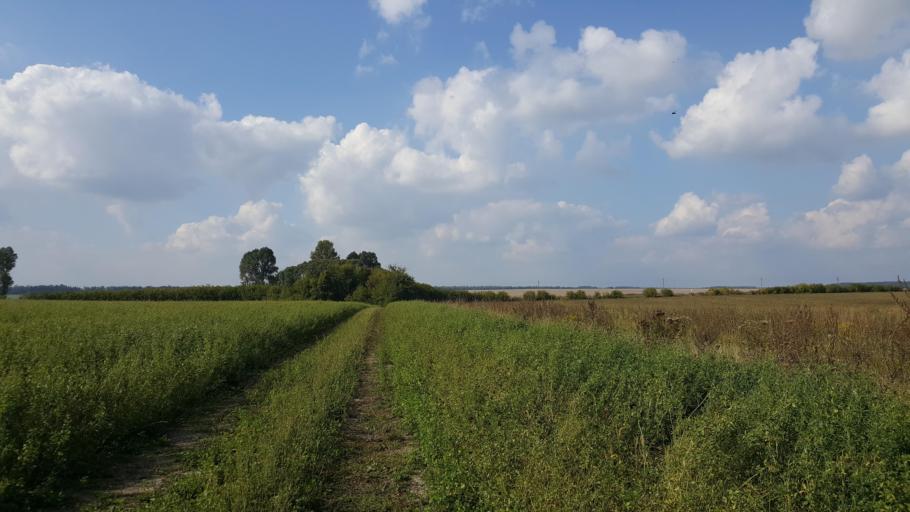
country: BY
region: Brest
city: Kamyanyets
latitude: 52.4213
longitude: 23.8115
